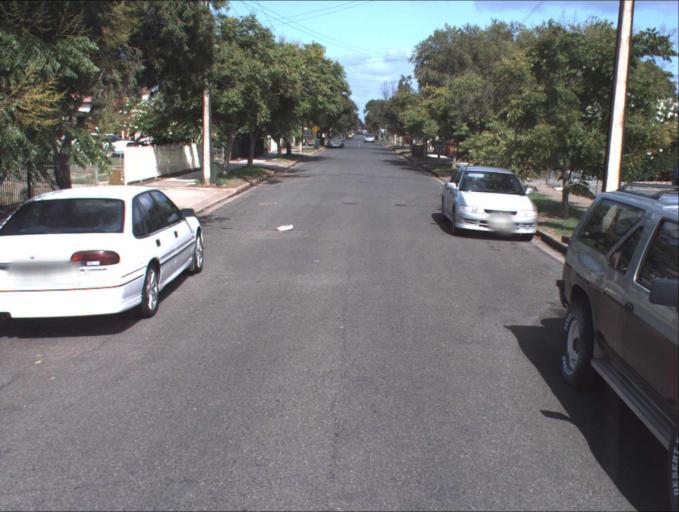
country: AU
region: South Australia
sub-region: Charles Sturt
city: Woodville North
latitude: -34.8712
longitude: 138.5534
